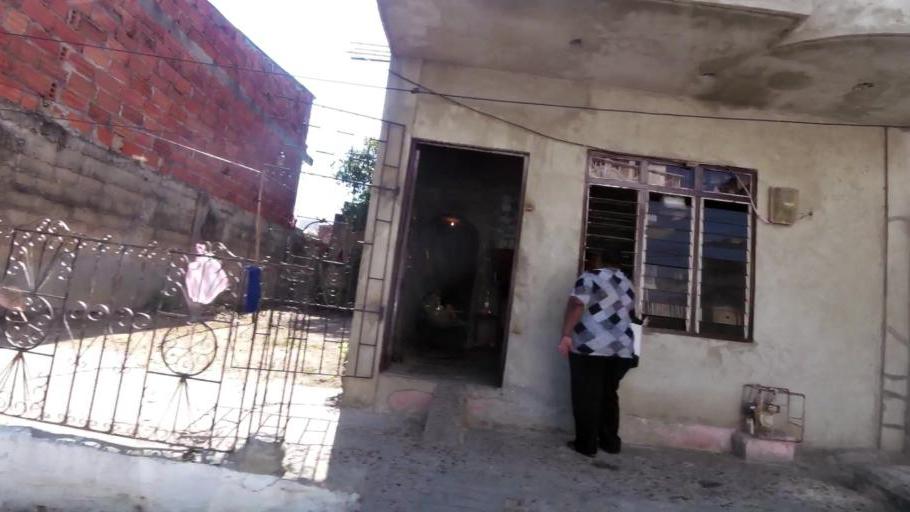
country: CO
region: Bolivar
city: Cartagena
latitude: 10.3963
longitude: -75.5095
